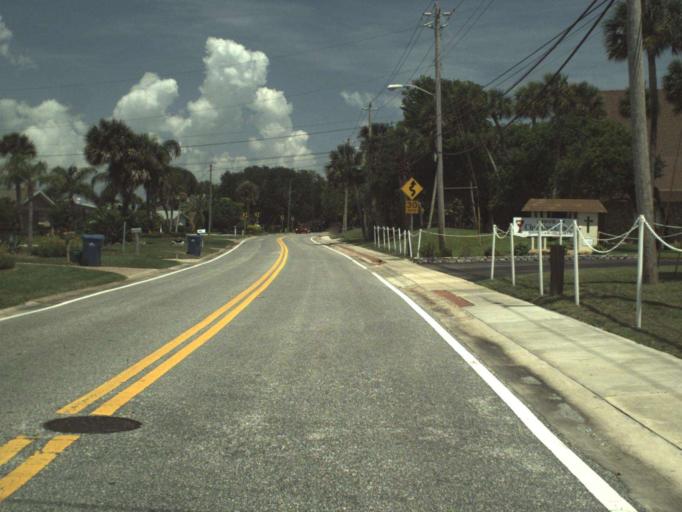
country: US
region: Florida
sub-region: Volusia County
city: Daytona Beach Shores
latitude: 29.1608
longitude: -80.9778
